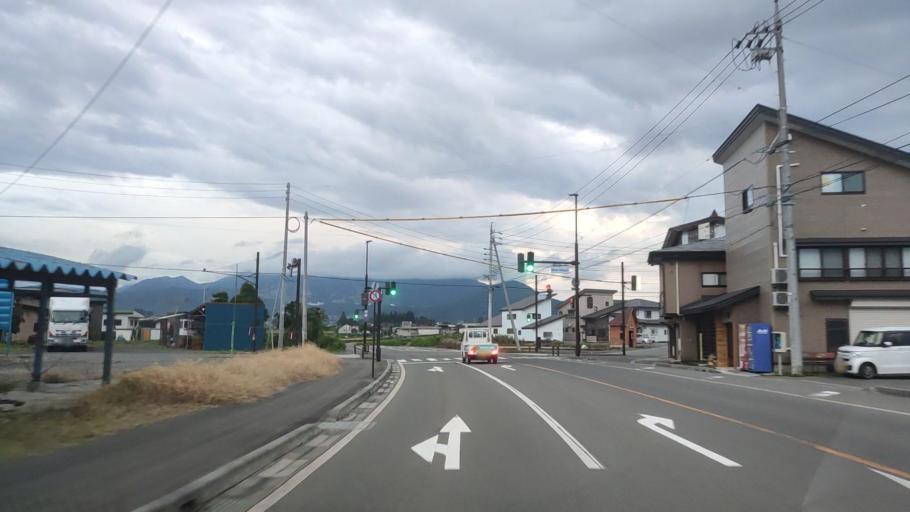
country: JP
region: Nagano
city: Iiyama
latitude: 36.8783
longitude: 138.4099
